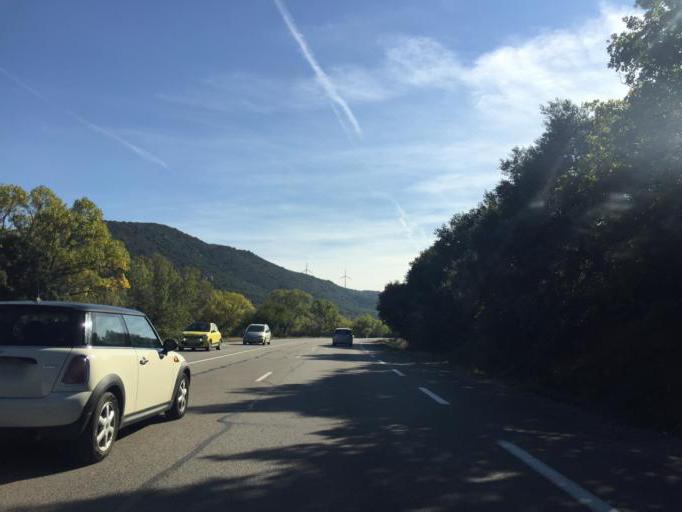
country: FR
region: Rhone-Alpes
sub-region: Departement de la Drome
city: Malataverne
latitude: 44.4766
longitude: 4.7643
